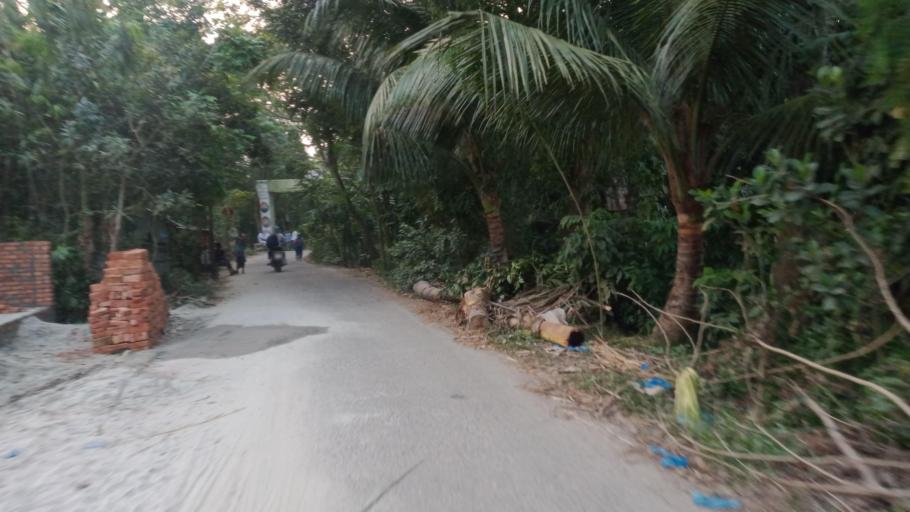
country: BD
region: Chittagong
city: Hajiganj
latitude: 23.3676
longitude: 90.9846
